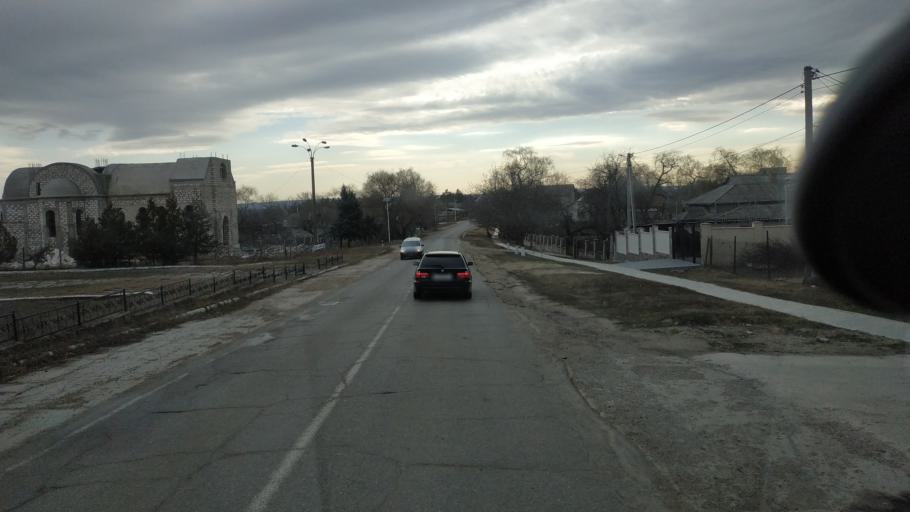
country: MD
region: Criuleni
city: Criuleni
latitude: 47.1642
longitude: 29.1208
